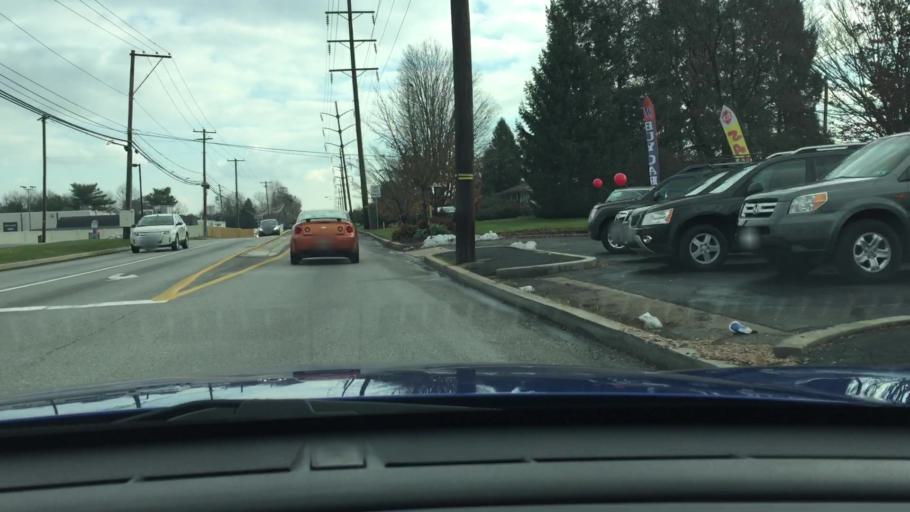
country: US
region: Pennsylvania
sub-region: Cumberland County
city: Shiremanstown
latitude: 40.2184
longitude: -76.9779
